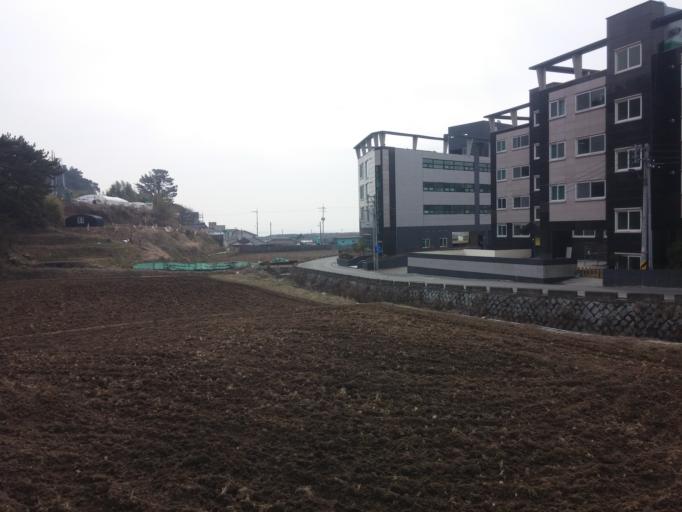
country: KR
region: Ulsan
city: Ulsan
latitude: 35.5865
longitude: 129.4561
